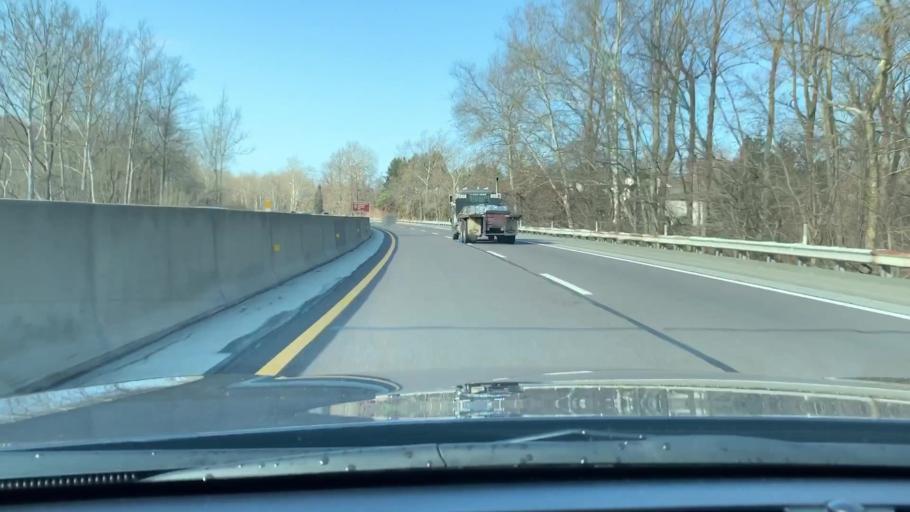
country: US
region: Pennsylvania
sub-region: Chester County
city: Chester Springs
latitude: 40.0645
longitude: -75.6339
